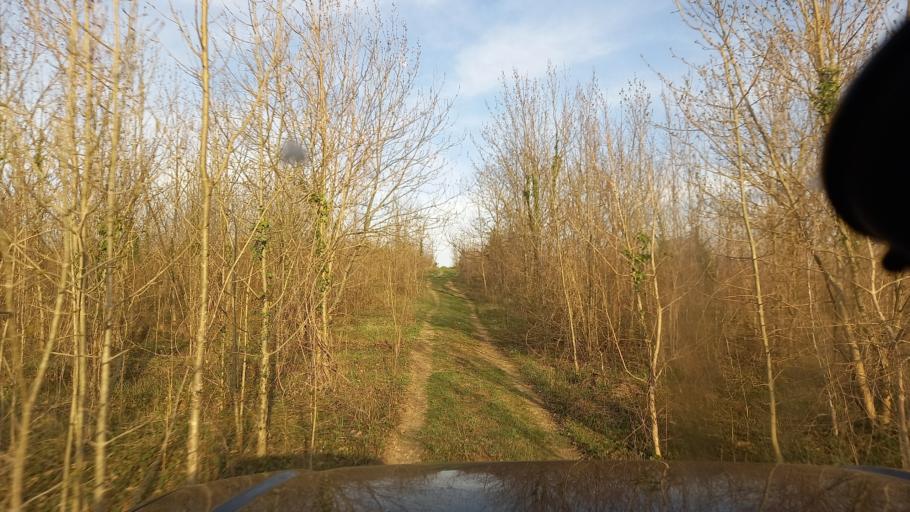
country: RU
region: Krasnodarskiy
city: Arkhipo-Osipovka
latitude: 44.3617
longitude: 38.5668
